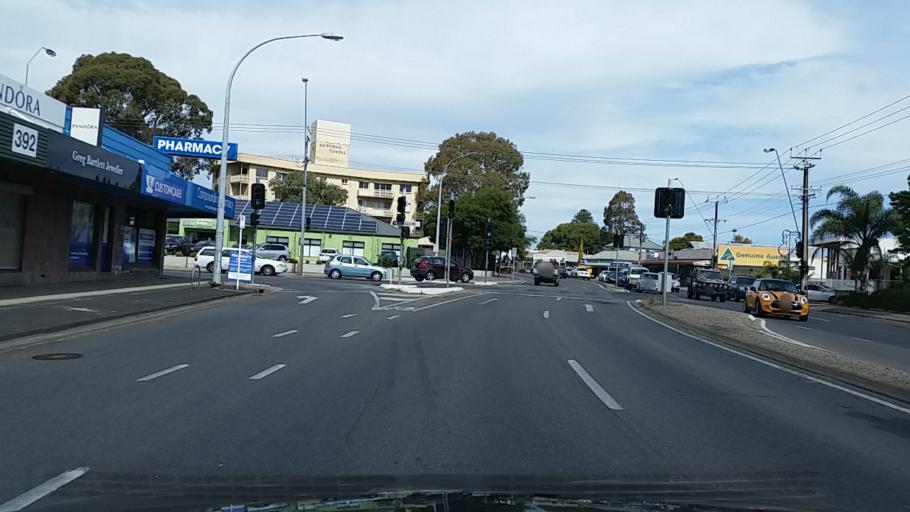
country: AU
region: South Australia
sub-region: Charles Sturt
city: Findon
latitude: -34.9267
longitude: 138.5345
